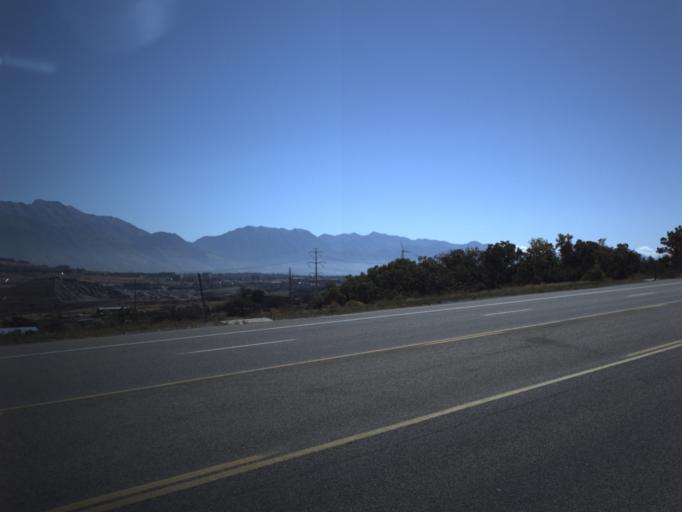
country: US
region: Utah
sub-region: Salt Lake County
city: Bluffdale
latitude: 40.4497
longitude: -111.9369
